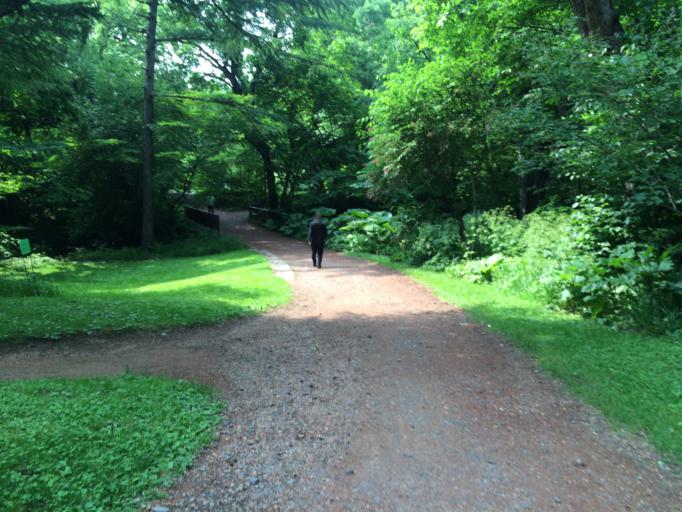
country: JP
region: Hokkaido
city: Sapporo
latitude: 43.0640
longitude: 141.3439
